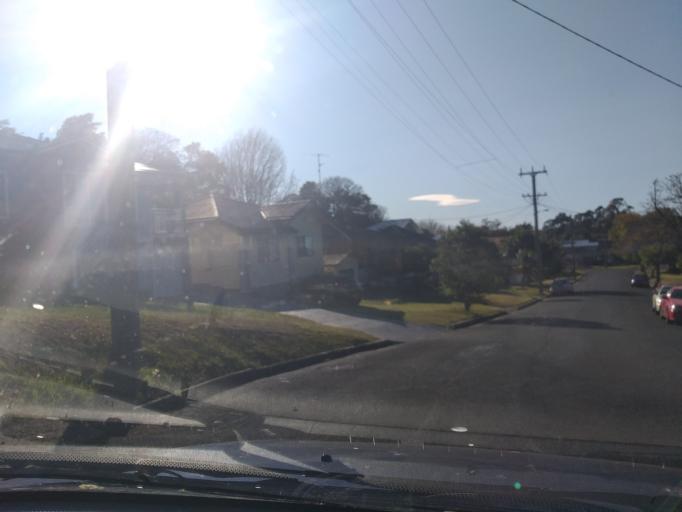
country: AU
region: New South Wales
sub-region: Wollongong
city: Bulli
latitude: -34.3186
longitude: 150.9118
